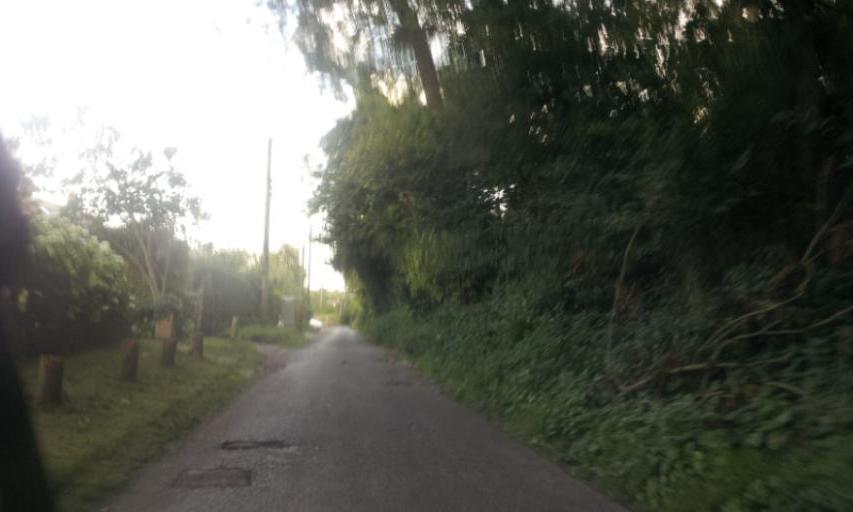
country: GB
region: England
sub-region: Kent
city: Meopham
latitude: 51.3786
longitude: 0.3940
